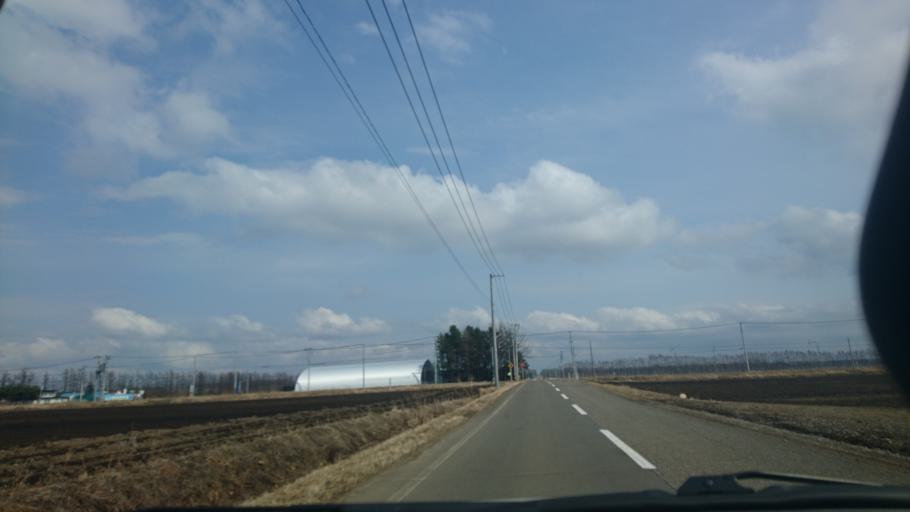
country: JP
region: Hokkaido
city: Otofuke
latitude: 43.2070
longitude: 143.2737
